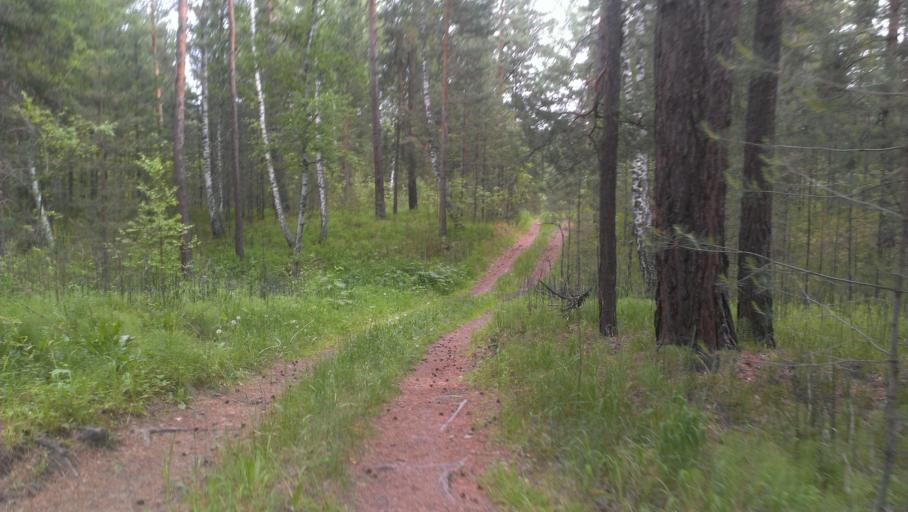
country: RU
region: Altai Krai
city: Sannikovo
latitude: 53.3492
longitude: 84.0377
